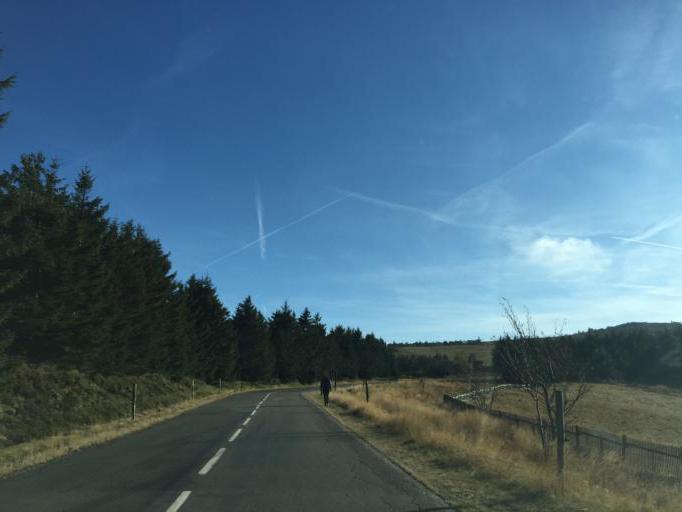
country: FR
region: Rhone-Alpes
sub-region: Departement de la Loire
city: Saint-Julien-Molin-Molette
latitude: 45.3886
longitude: 4.5762
